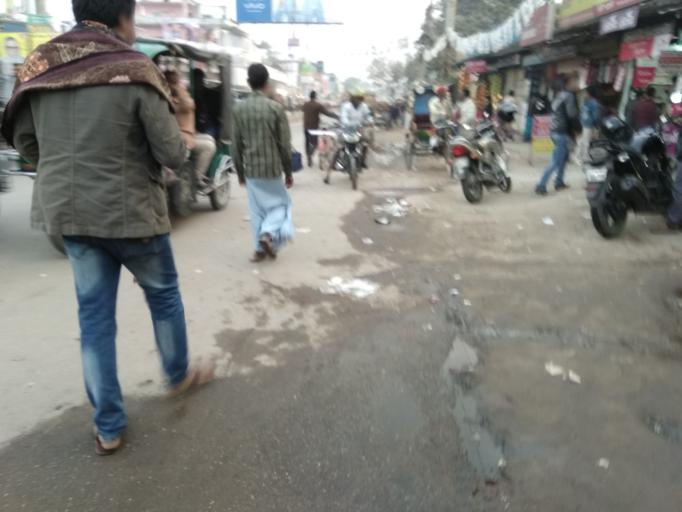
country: BD
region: Rangpur Division
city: Rangpur
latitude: 25.7403
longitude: 89.2543
